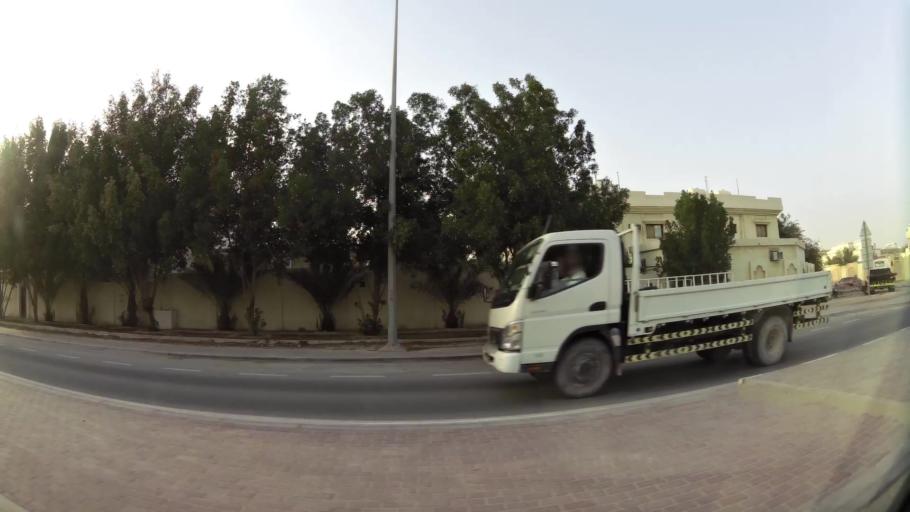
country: QA
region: Baladiyat ar Rayyan
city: Ar Rayyan
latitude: 25.2502
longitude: 51.4458
